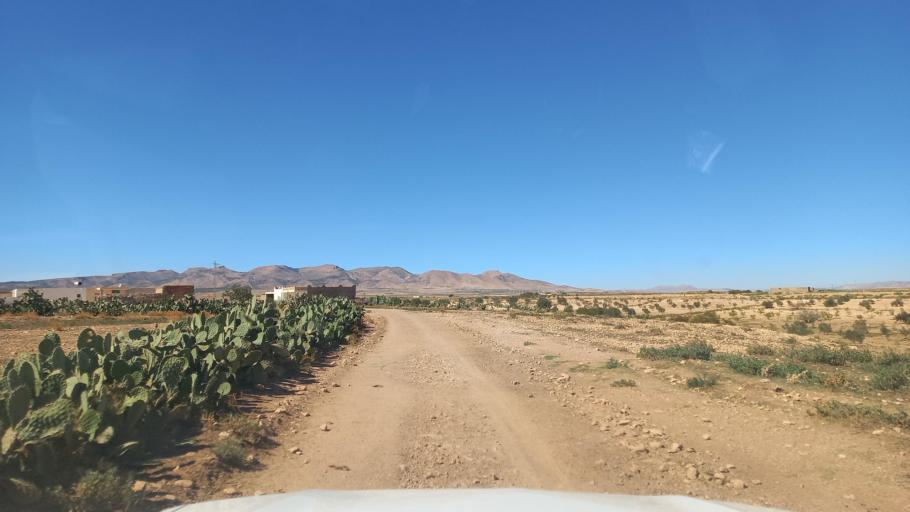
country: TN
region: Al Qasrayn
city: Sbiba
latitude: 35.3805
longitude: 9.0891
